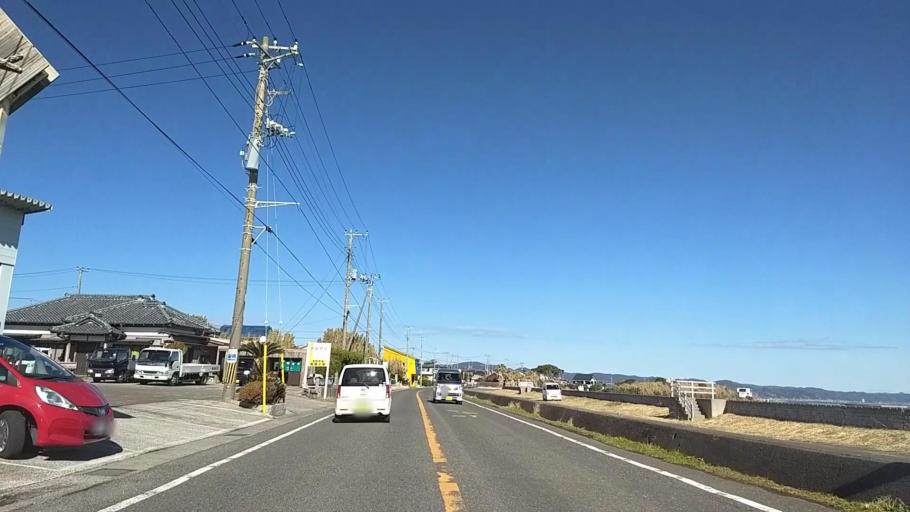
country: JP
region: Chiba
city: Tateyama
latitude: 34.9796
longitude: 139.9665
